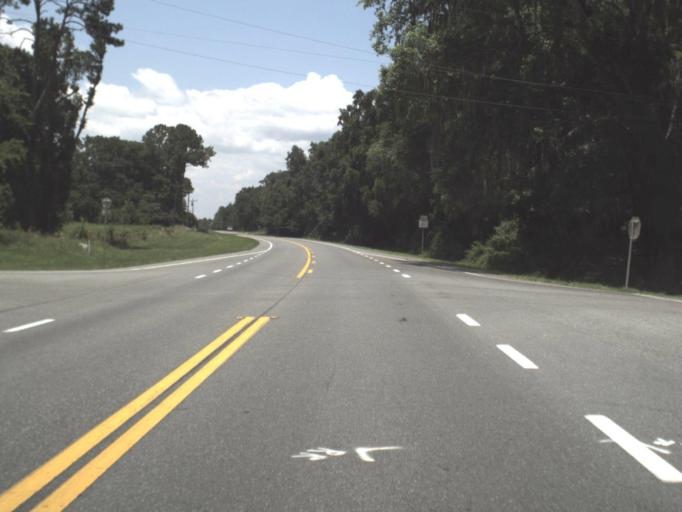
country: US
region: Florida
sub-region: Levy County
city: Williston
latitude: 29.4410
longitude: -82.4111
